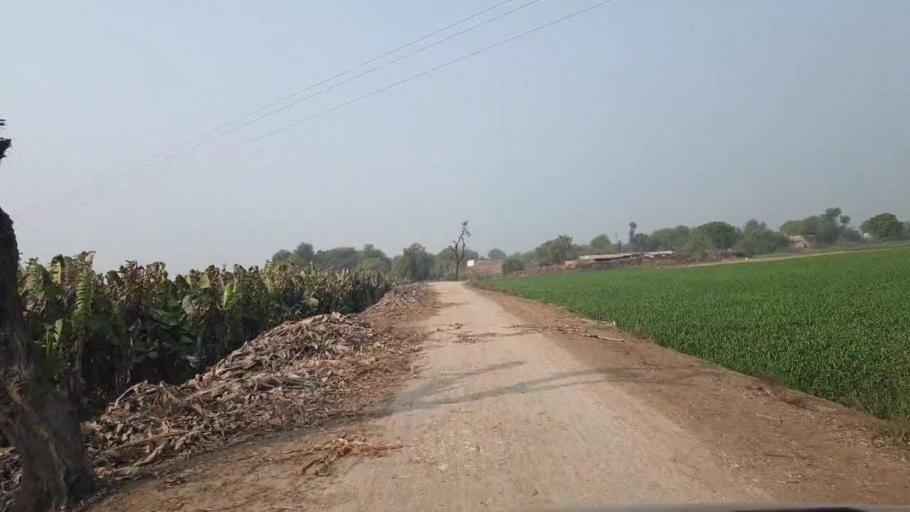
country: PK
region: Sindh
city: Hala
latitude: 25.8827
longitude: 68.3610
